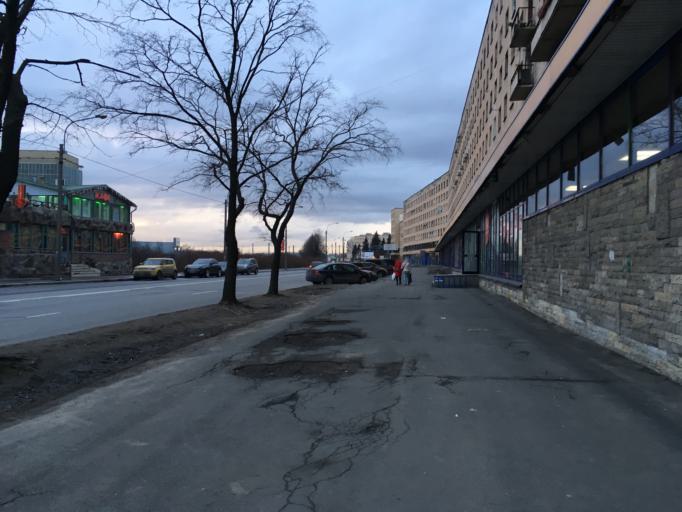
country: RU
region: St.-Petersburg
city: Centralniy
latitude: 59.9399
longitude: 30.4146
